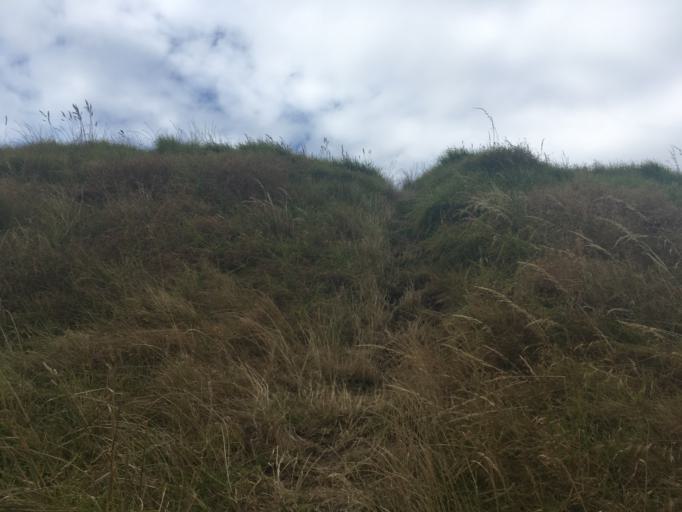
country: NZ
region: Auckland
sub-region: Auckland
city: Auckland
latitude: -36.8260
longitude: 174.7992
